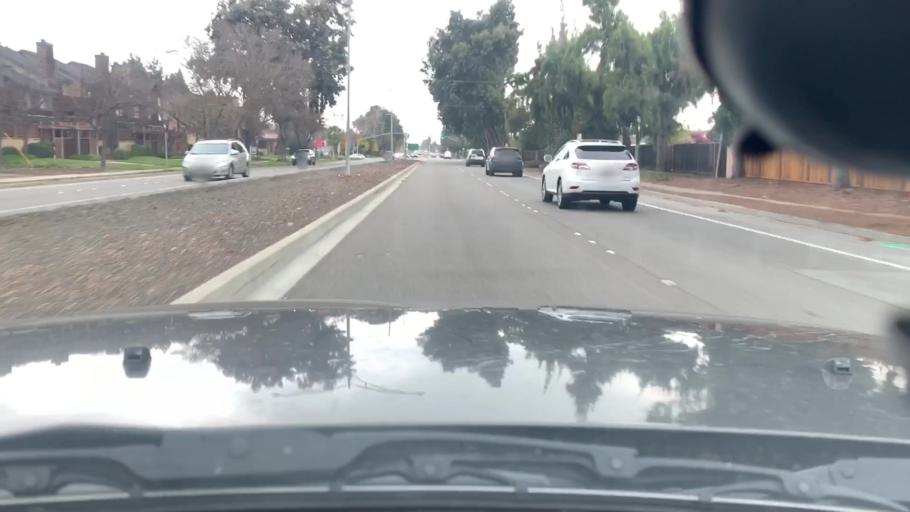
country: US
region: California
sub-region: Alameda County
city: Fremont
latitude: 37.5147
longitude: -121.9663
